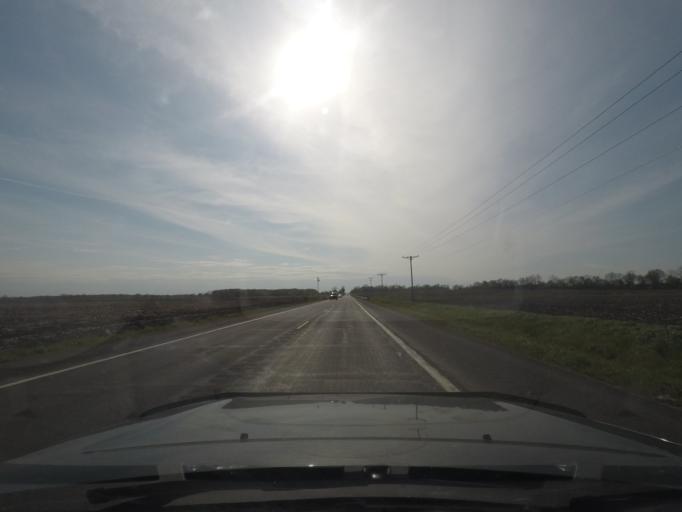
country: US
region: Michigan
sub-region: Berrien County
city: Three Oaks
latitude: 41.7984
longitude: -86.5591
